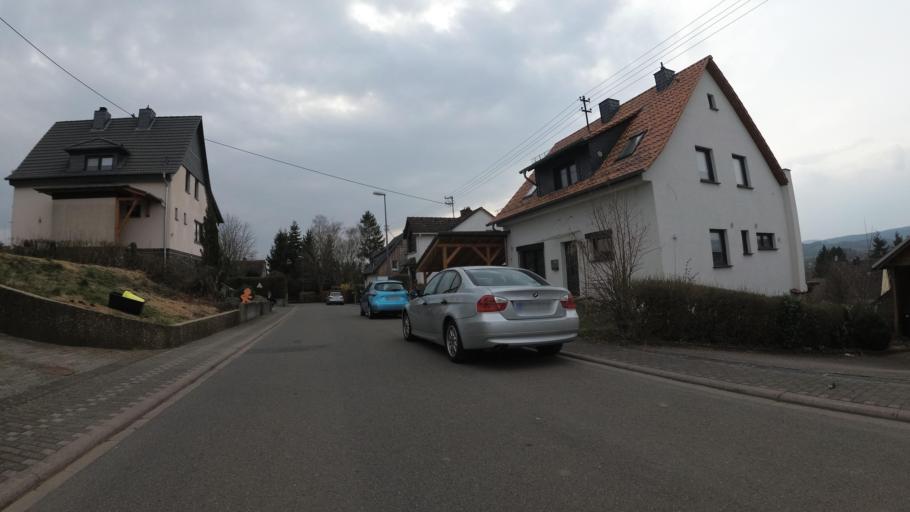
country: DE
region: Rheinland-Pfalz
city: Birkenfeld
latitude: 49.6512
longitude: 7.1616
